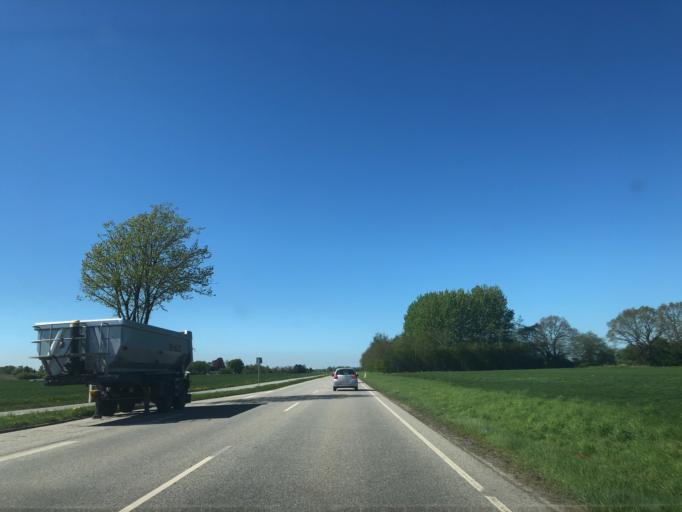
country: DK
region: Zealand
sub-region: Stevns Kommune
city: Store Heddinge
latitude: 55.3445
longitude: 12.3380
